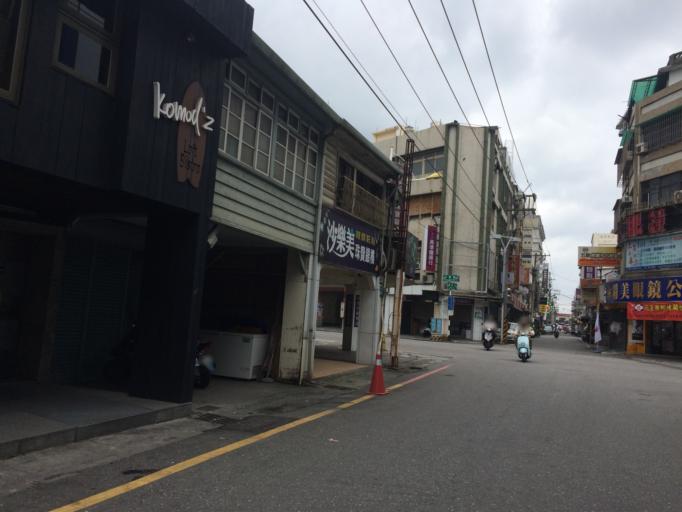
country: TW
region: Taiwan
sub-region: Hualien
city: Hualian
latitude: 23.9762
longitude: 121.6072
